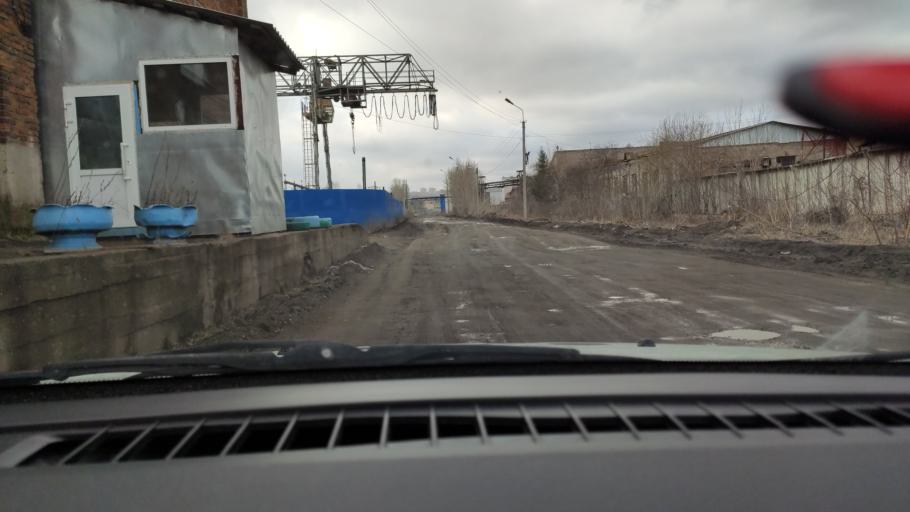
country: RU
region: Perm
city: Perm
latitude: 58.0486
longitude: 56.3175
